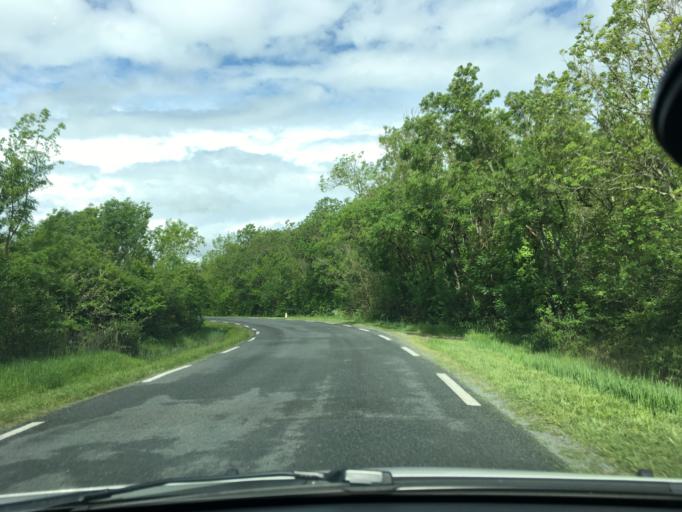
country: FR
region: Aquitaine
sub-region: Departement de la Gironde
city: Saint-Estephe
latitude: 45.3200
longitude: -0.8088
